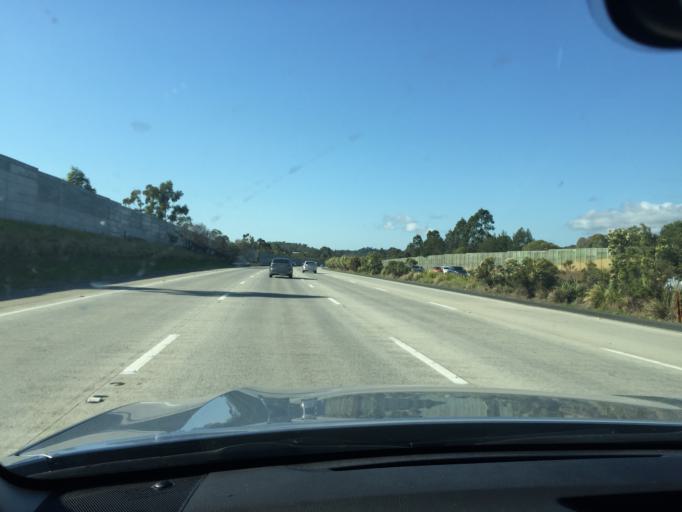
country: AU
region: Queensland
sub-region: Gold Coast
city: Ormeau Hills
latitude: -27.7883
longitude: 153.2579
